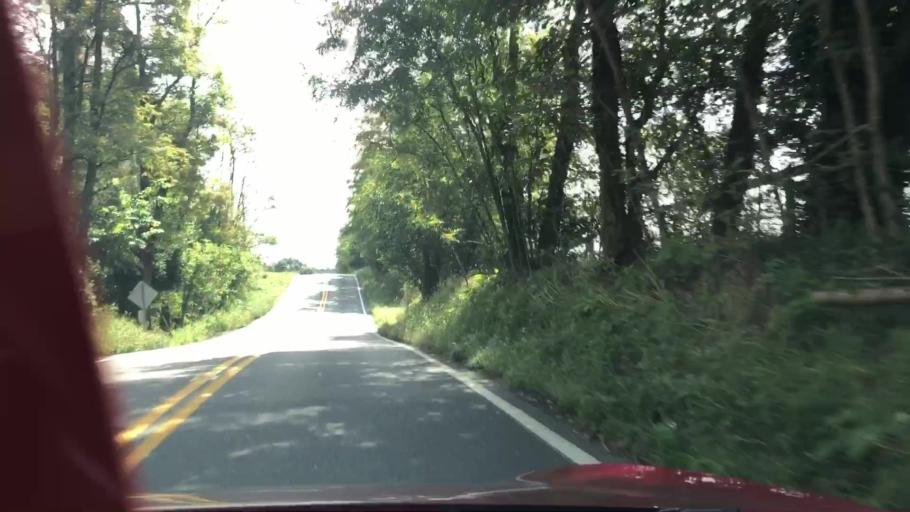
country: US
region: Pennsylvania
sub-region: Dauphin County
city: Skyline View
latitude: 40.3514
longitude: -76.6735
